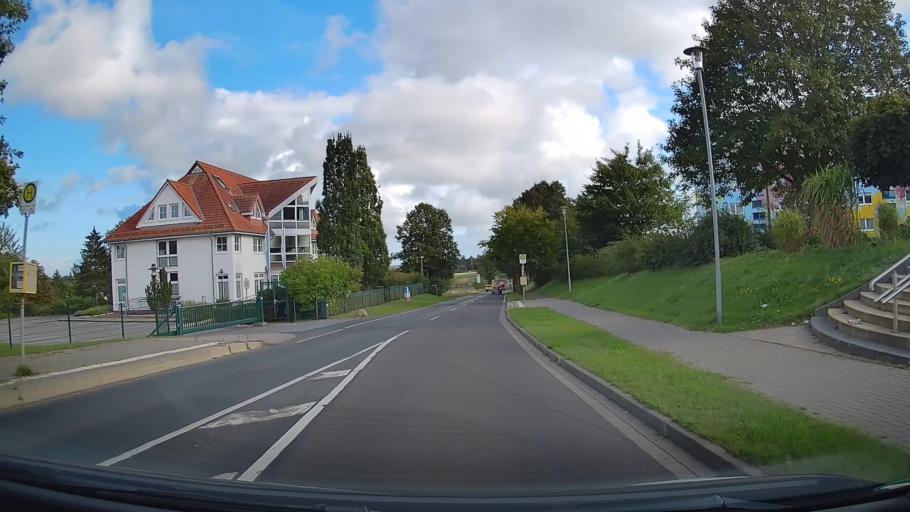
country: DE
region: Mecklenburg-Vorpommern
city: Bergen auf Ruegen
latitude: 54.4112
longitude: 13.4381
